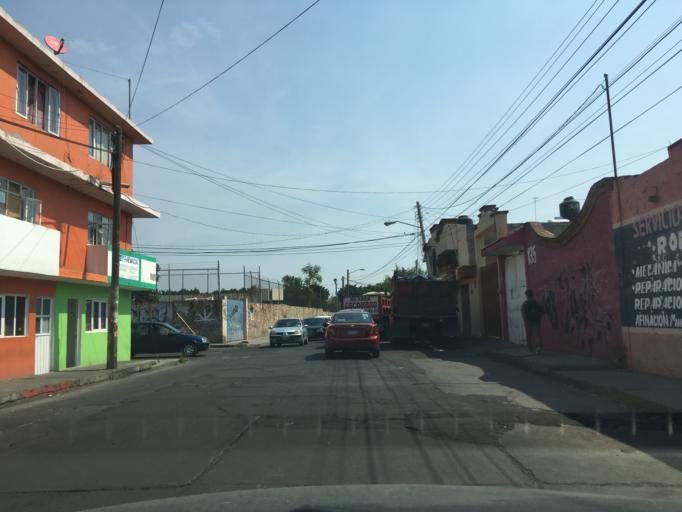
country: MX
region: Michoacan
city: Morelia
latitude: 19.6937
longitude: -101.2033
